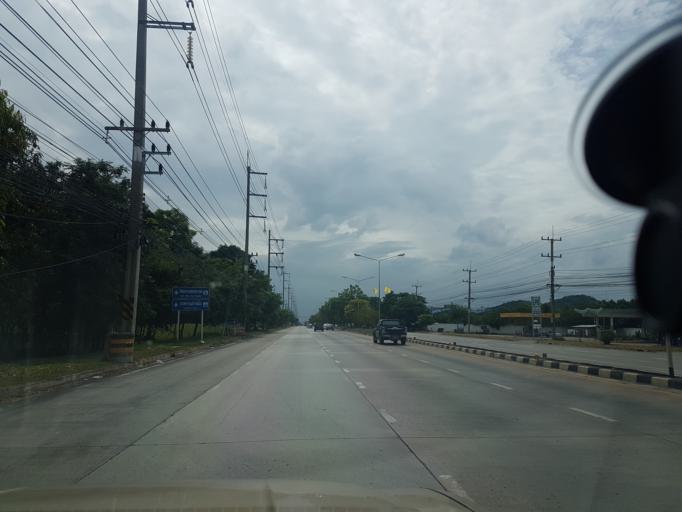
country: TH
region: Sara Buri
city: Phra Phutthabat
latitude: 14.7163
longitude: 100.8159
